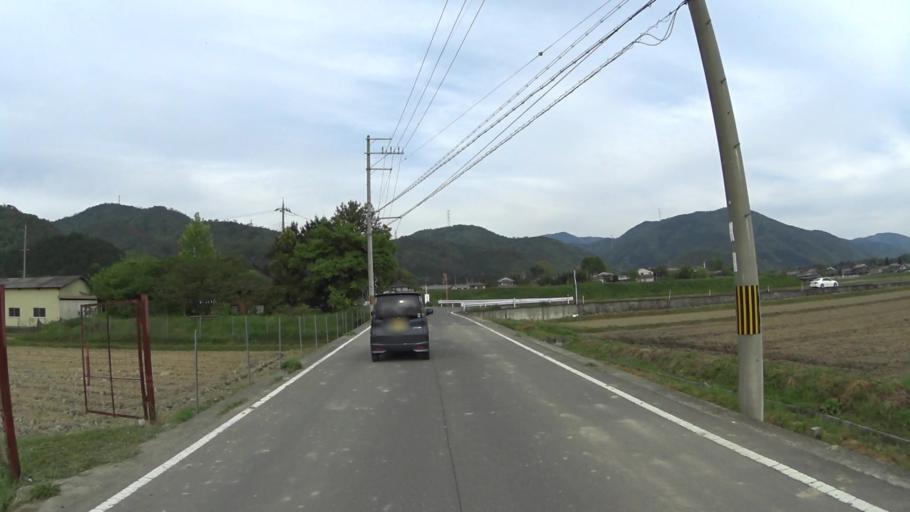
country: JP
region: Kyoto
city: Kameoka
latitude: 35.0914
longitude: 135.5506
